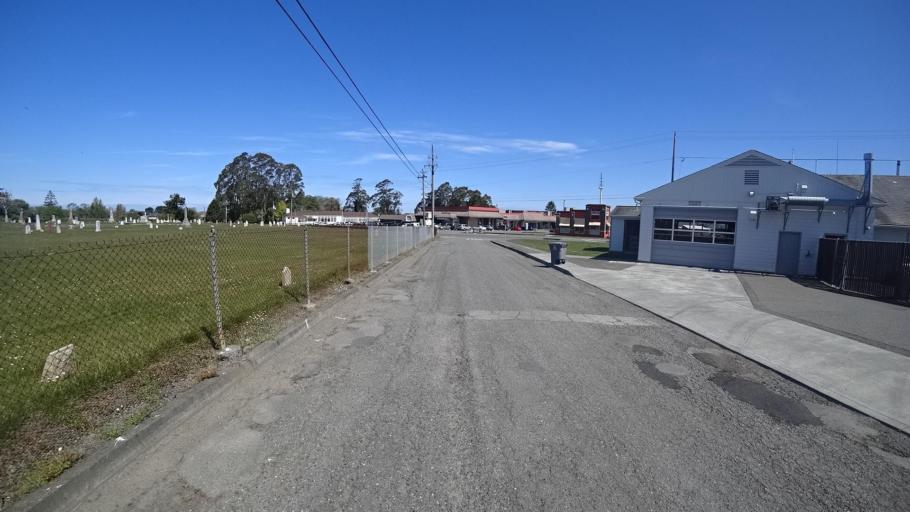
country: US
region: California
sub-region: Humboldt County
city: Eureka
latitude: 40.7994
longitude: -124.1491
